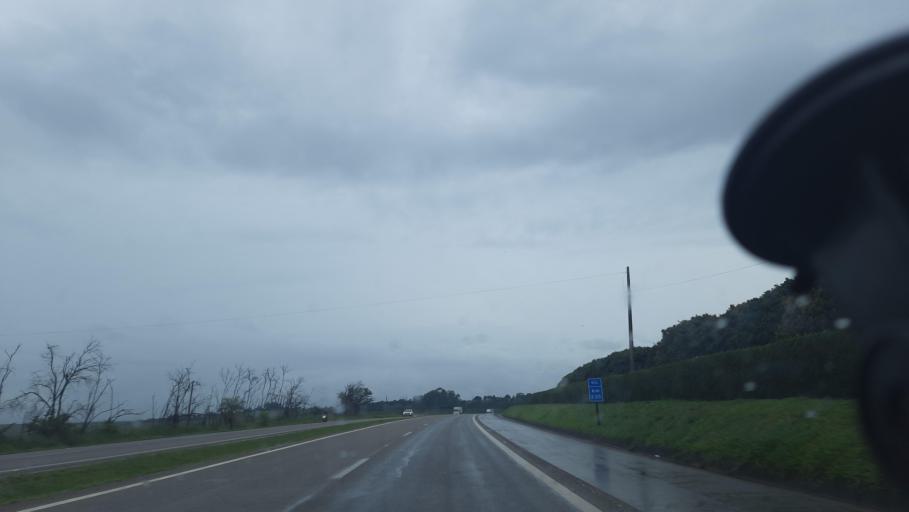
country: BR
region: Sao Paulo
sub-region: Casa Branca
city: Casa Branca
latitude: -21.7961
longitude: -47.0600
